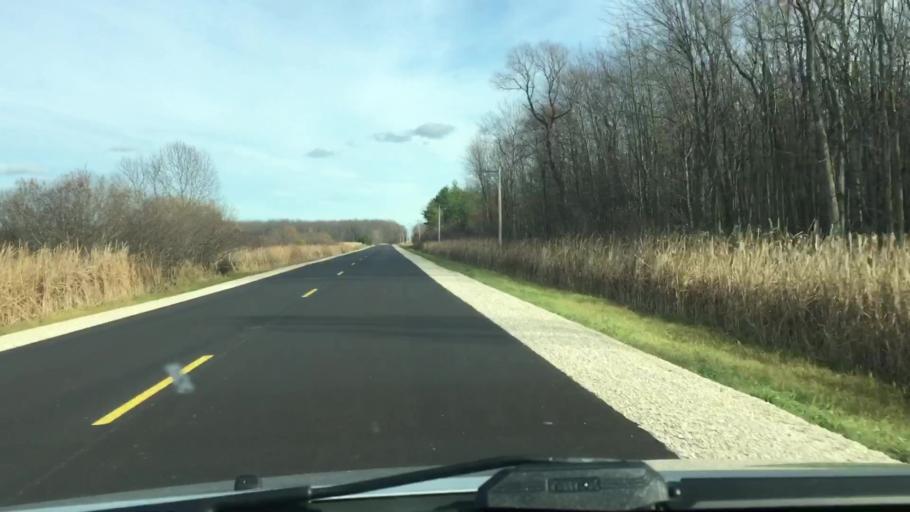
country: US
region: Wisconsin
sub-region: Kewaunee County
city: Algoma
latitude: 44.6899
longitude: -87.5359
